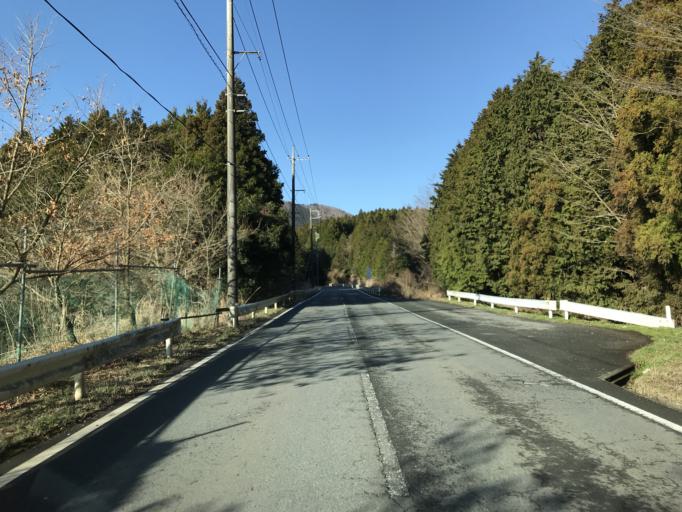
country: JP
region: Shizuoka
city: Gotemba
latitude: 35.2630
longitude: 138.8466
